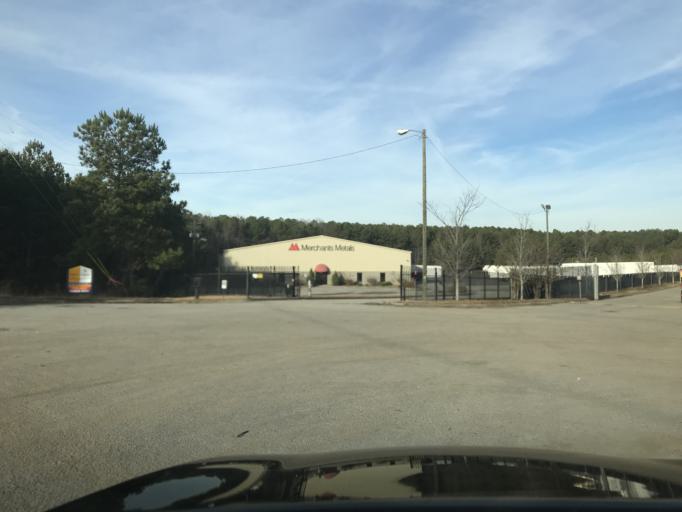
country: US
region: Georgia
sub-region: Clayton County
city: Morrow
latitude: 33.5599
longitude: -84.3564
